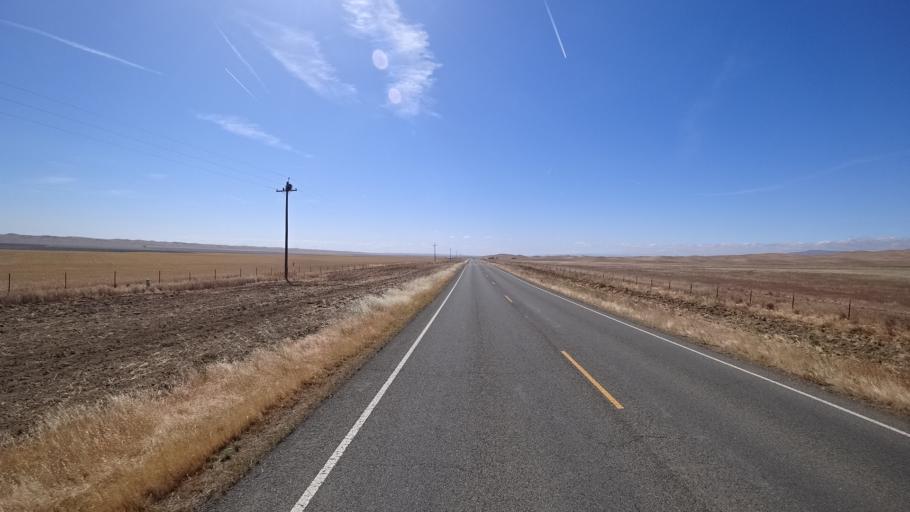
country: US
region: California
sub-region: Kings County
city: Avenal
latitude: 35.9257
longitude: -120.0771
